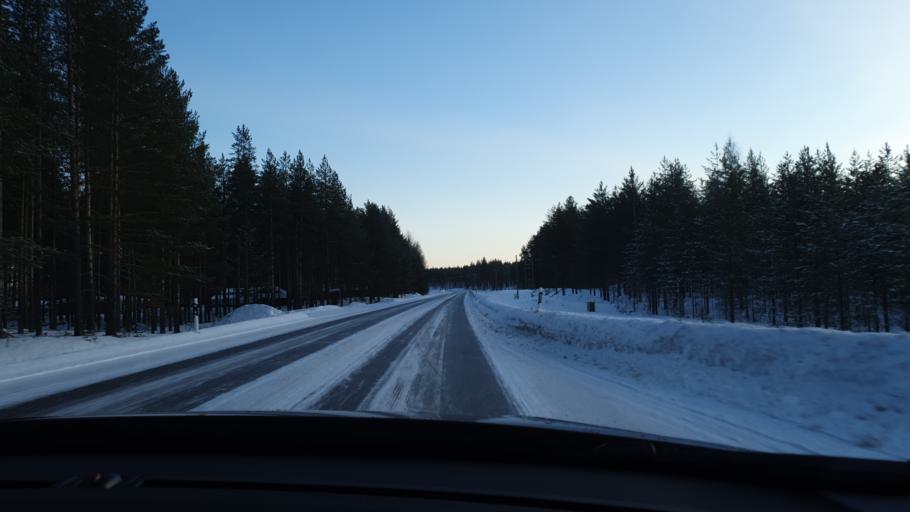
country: FI
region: Kainuu
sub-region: Kajaani
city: Sotkamo
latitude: 64.0954
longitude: 28.5472
